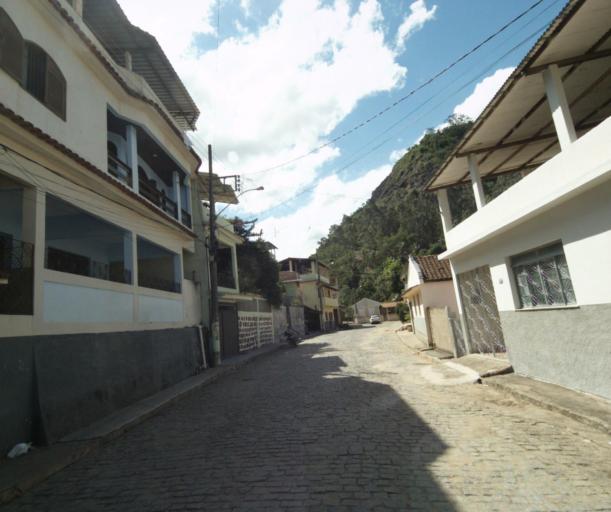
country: BR
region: Espirito Santo
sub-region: Mimoso Do Sul
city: Mimoso do Sul
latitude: -21.0573
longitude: -41.3635
